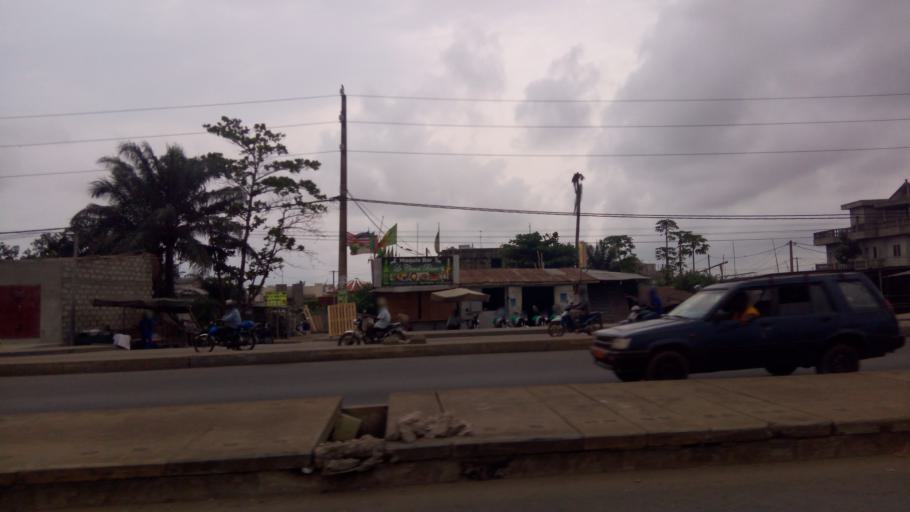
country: BJ
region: Littoral
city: Cotonou
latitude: 6.3776
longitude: 2.3825
